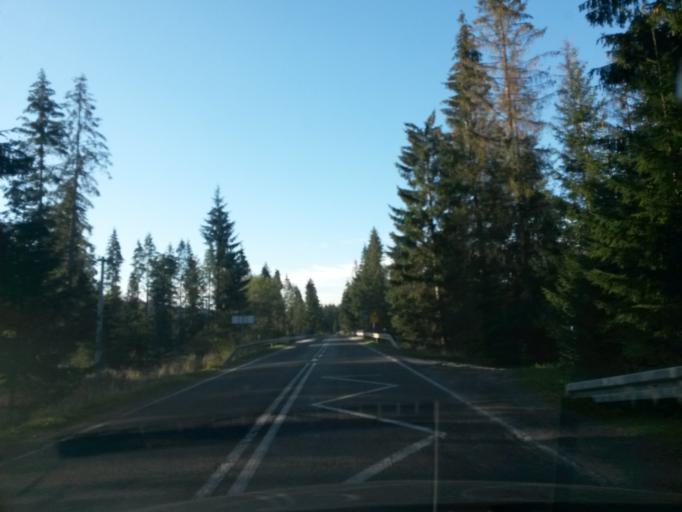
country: PL
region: Lesser Poland Voivodeship
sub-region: Powiat tatrzanski
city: Koscielisko
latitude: 49.2901
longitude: 19.8501
